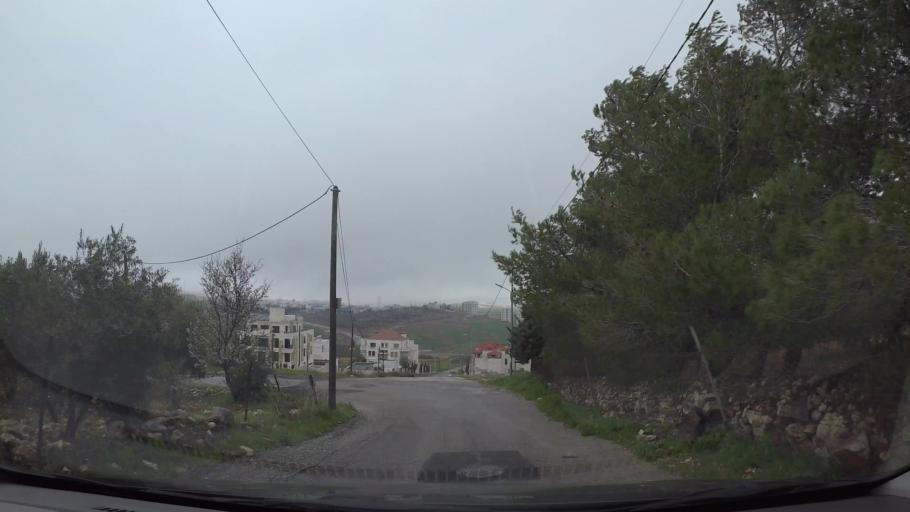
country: JO
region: Amman
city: Umm as Summaq
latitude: 31.9153
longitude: 35.8654
